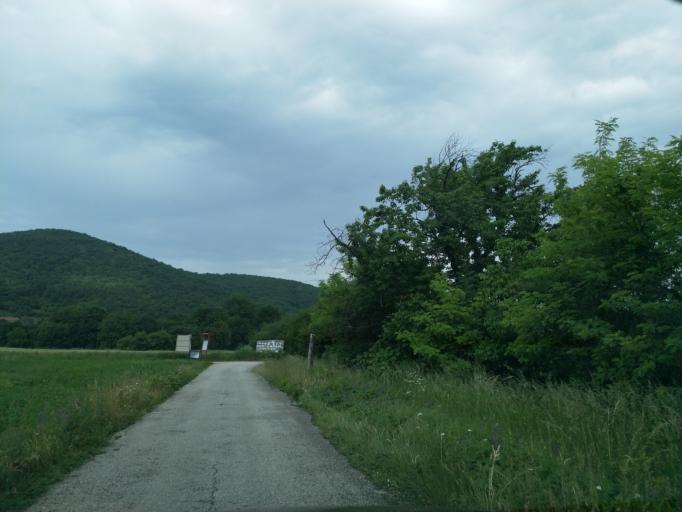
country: RS
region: Central Serbia
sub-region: Borski Okrug
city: Bor
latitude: 44.0291
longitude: 21.9663
